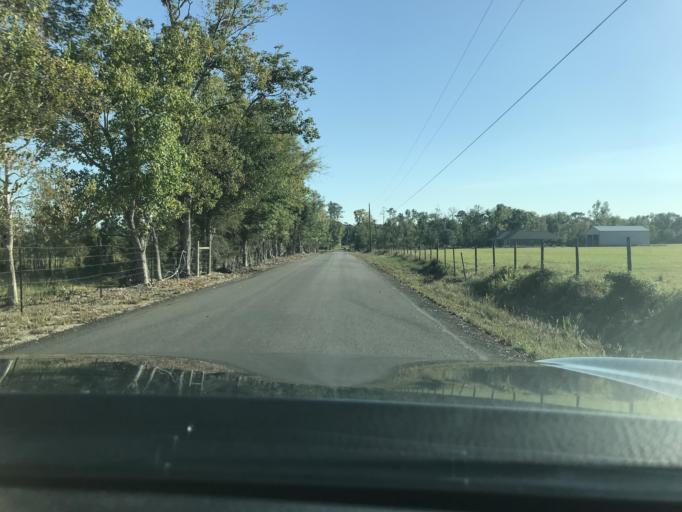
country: US
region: Louisiana
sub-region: Calcasieu Parish
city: Westlake
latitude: 30.3141
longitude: -93.2668
